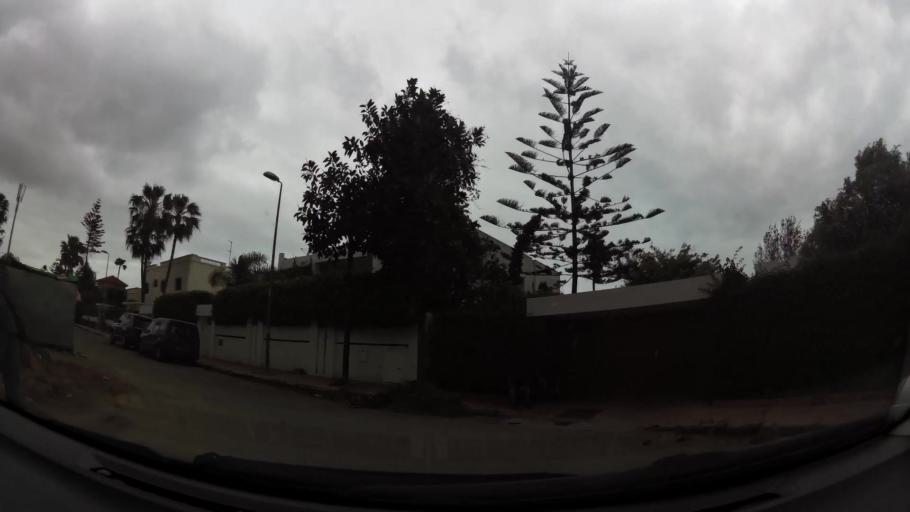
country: MA
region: Grand Casablanca
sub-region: Casablanca
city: Casablanca
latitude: 33.5796
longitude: -7.6654
